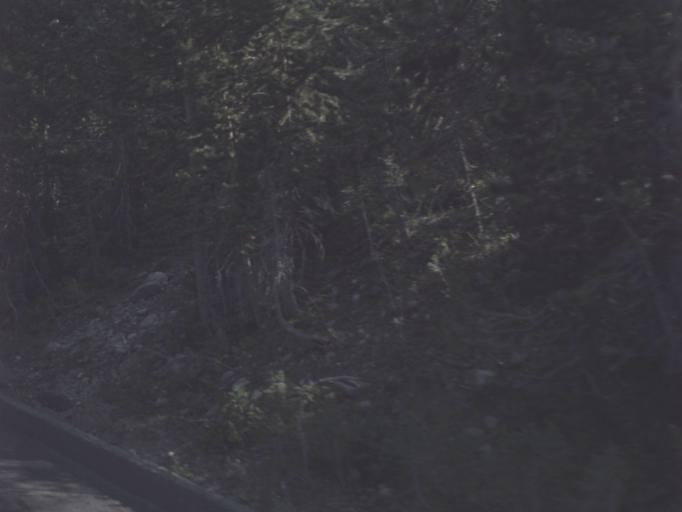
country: US
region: Utah
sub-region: Summit County
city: Kamas
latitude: 40.7526
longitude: -110.8776
